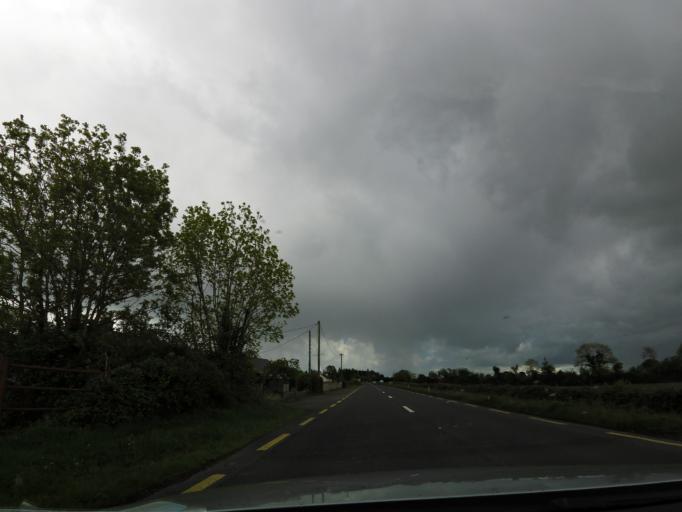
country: IE
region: Munster
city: Thurles
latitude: 52.7154
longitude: -7.8264
